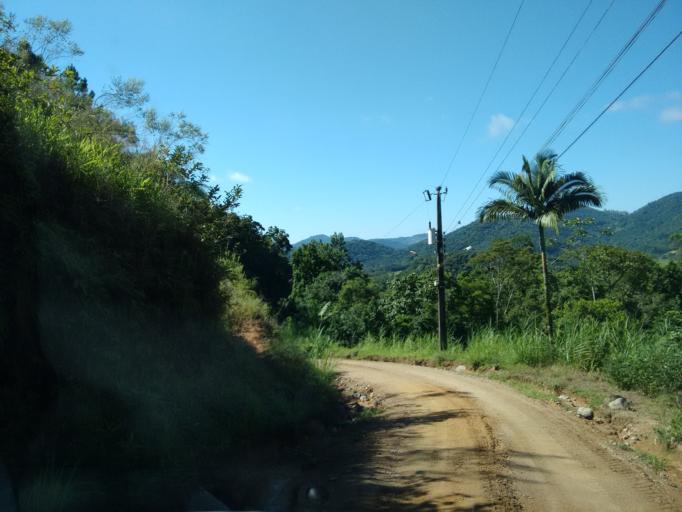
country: BR
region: Santa Catarina
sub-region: Pomerode
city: Pomerode
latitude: -26.7590
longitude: -49.1918
